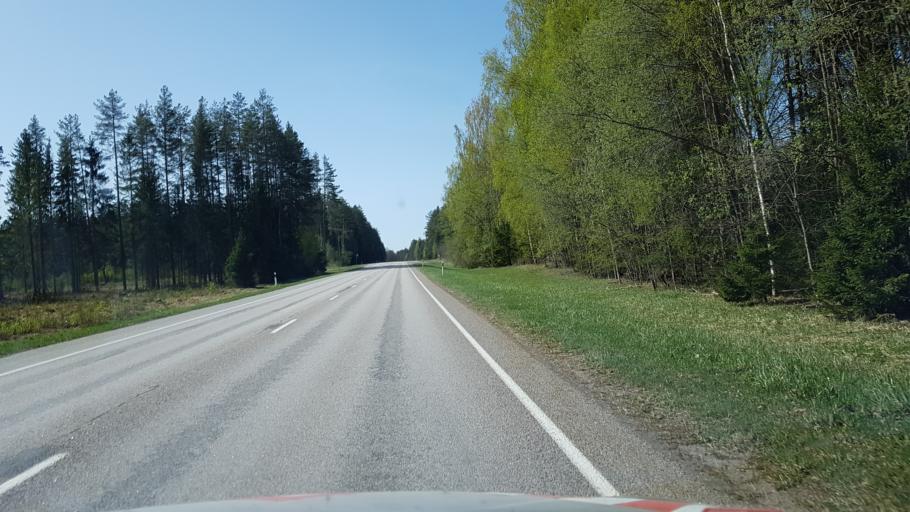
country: EE
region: Valgamaa
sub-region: Valga linn
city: Valga
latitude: 57.8243
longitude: 26.0523
